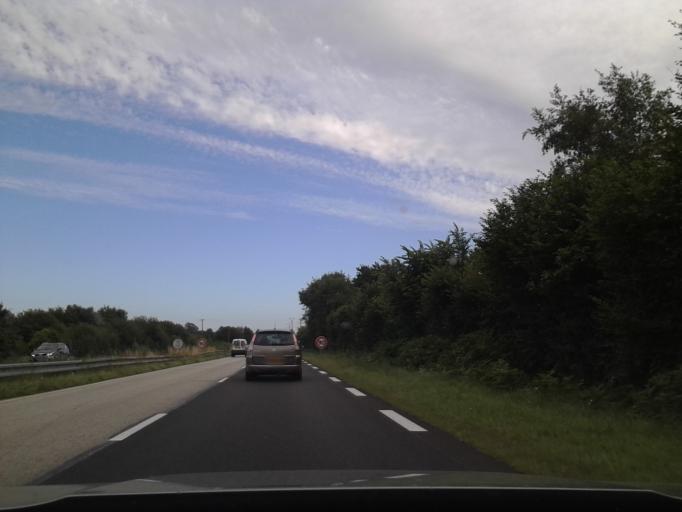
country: FR
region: Lower Normandy
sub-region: Departement de la Manche
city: Brix
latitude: 49.5752
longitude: -1.5791
